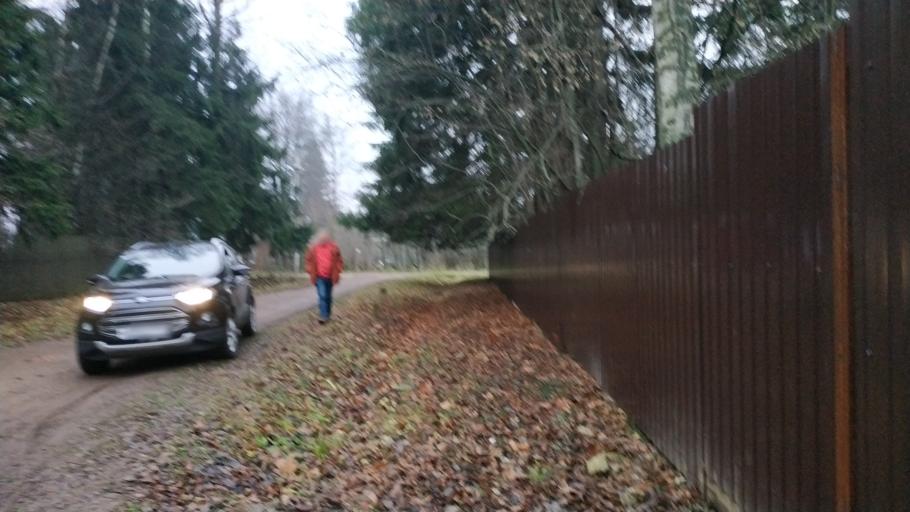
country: RU
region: Moskovskaya
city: Lugovaya
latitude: 56.0565
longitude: 37.4760
